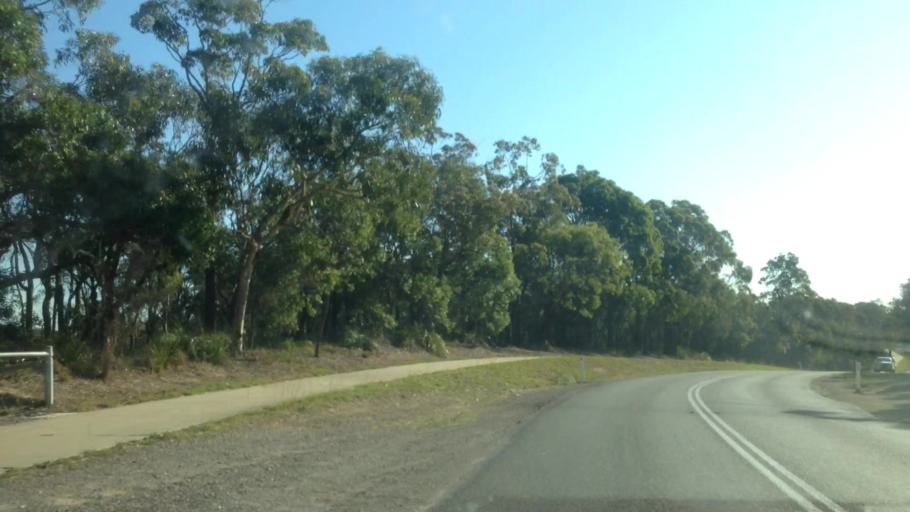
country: AU
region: New South Wales
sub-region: Lake Macquarie Shire
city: Dora Creek
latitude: -33.1083
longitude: 151.5391
